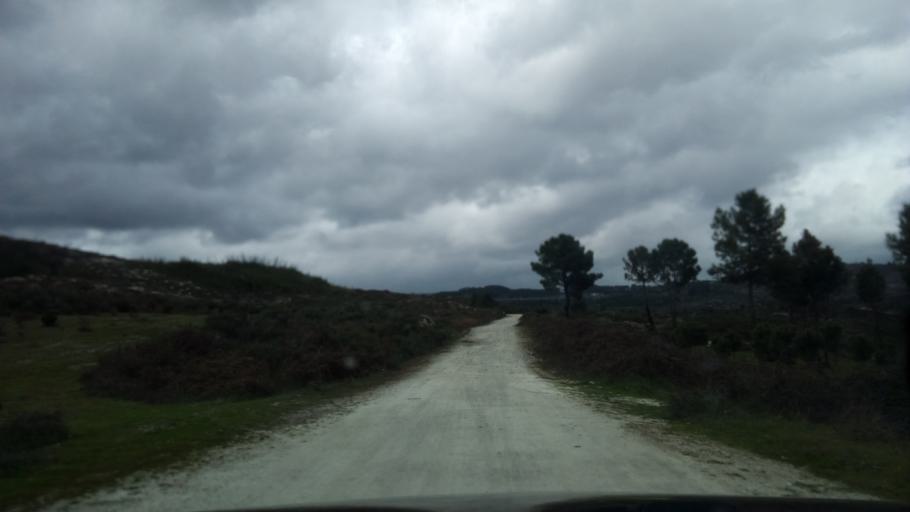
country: PT
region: Guarda
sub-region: Fornos de Algodres
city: Fornos de Algodres
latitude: 40.5908
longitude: -7.5671
